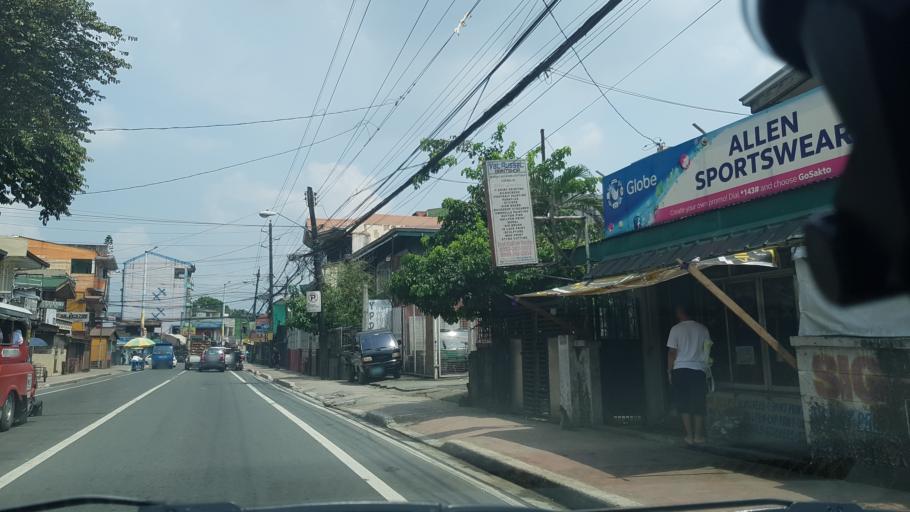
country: PH
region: Calabarzon
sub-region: Province of Rizal
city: Antipolo
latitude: 14.6566
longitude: 121.1036
